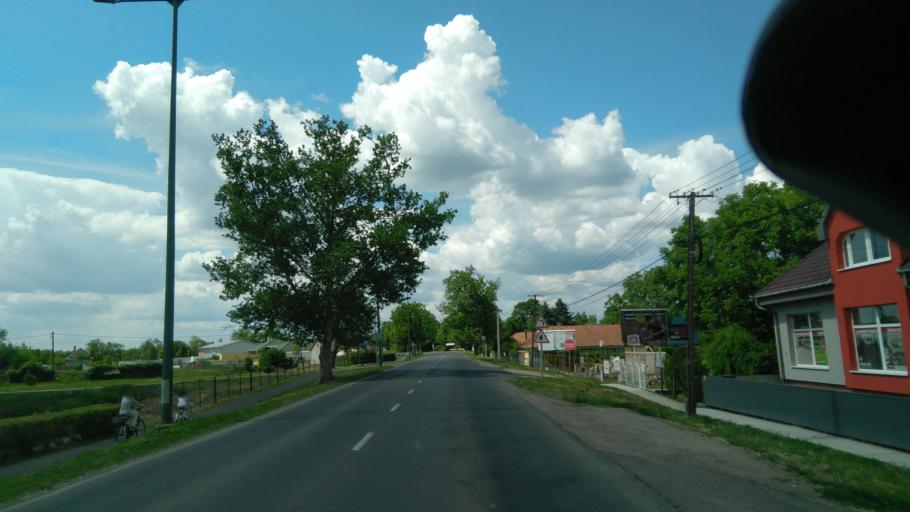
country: HU
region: Bekes
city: Gyula
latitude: 46.6507
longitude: 21.2474
